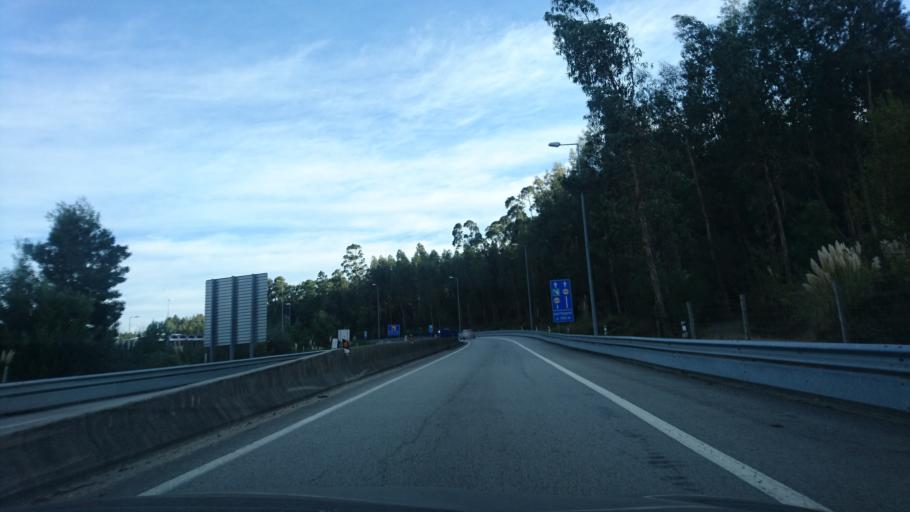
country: PT
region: Aveiro
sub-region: Santa Maria da Feira
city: Milheiros de Poiares
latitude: 40.9389
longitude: -8.4740
